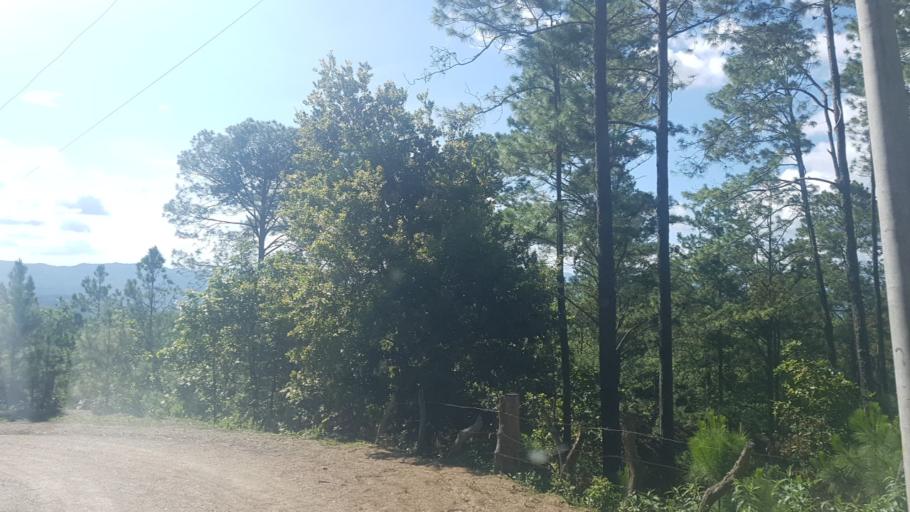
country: NI
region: Madriz
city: Somoto
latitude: 13.6385
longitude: -86.6462
